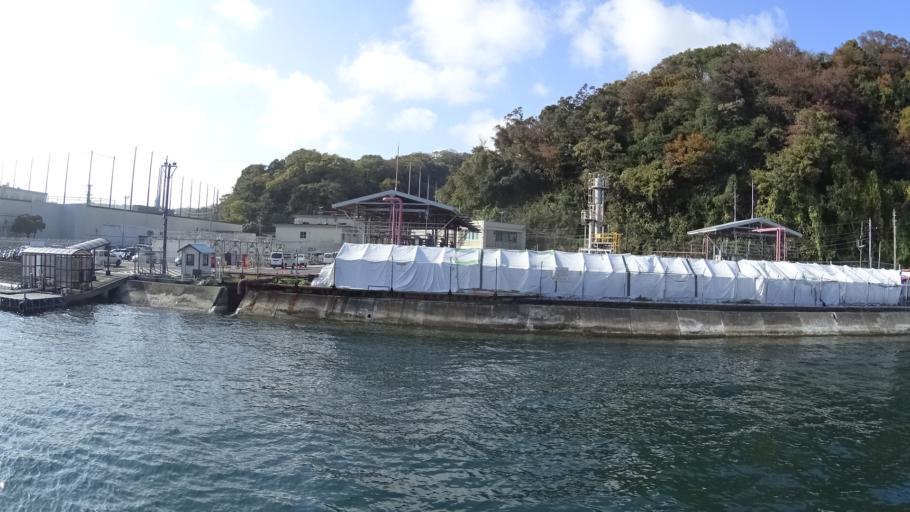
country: JP
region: Kanagawa
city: Yokosuka
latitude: 35.2951
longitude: 139.6475
